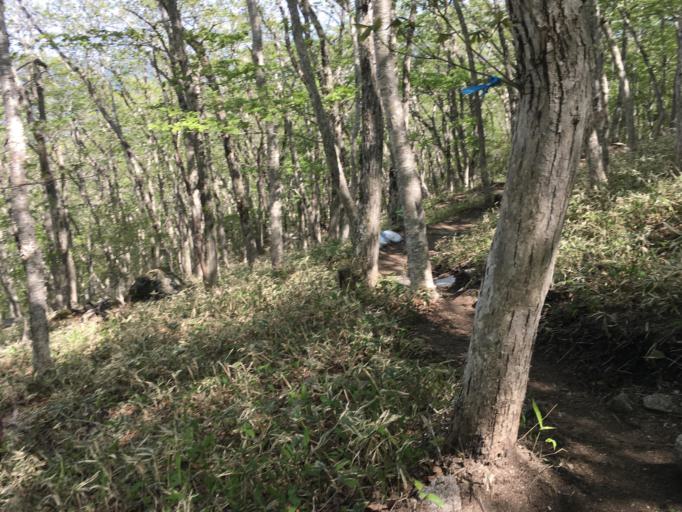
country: JP
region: Iwate
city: Ofunato
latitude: 39.1896
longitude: 141.7309
